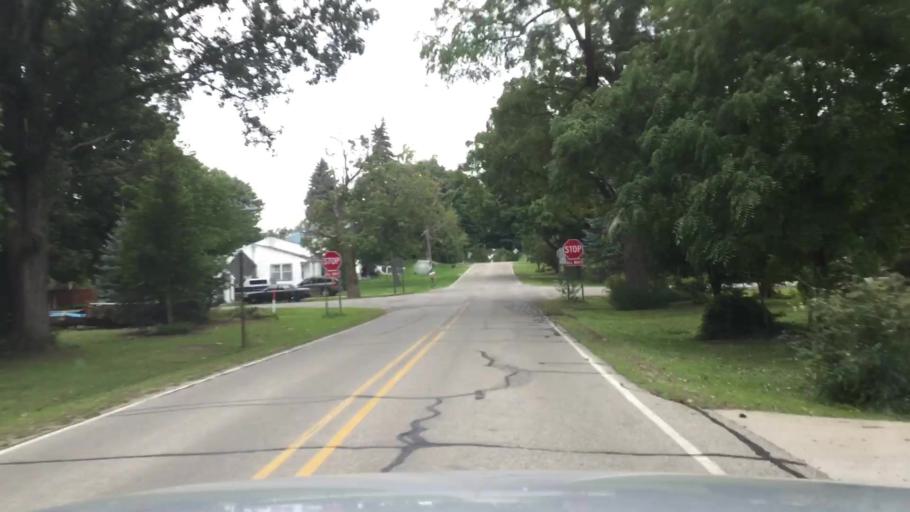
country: US
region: Michigan
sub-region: Shiawassee County
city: Durand
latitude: 42.9101
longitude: -84.0695
